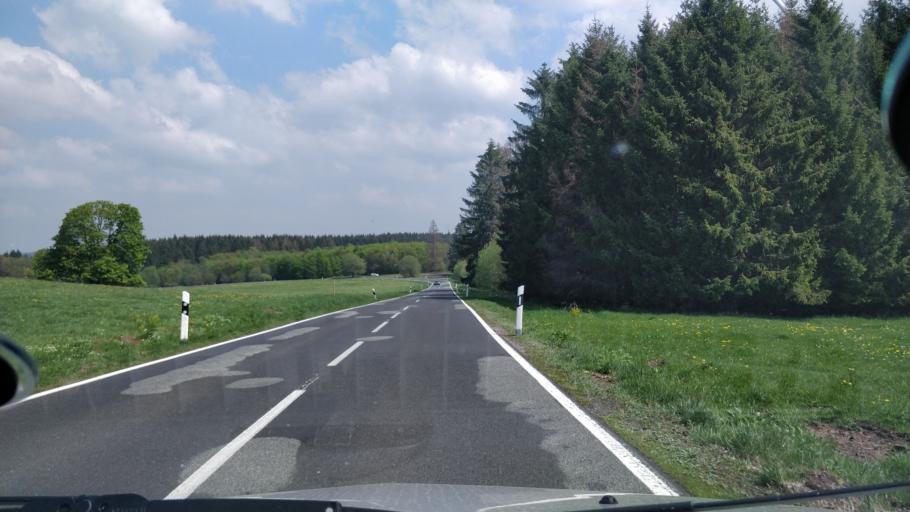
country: DE
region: Rheinland-Pfalz
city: Hohn
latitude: 50.6285
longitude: 7.9972
